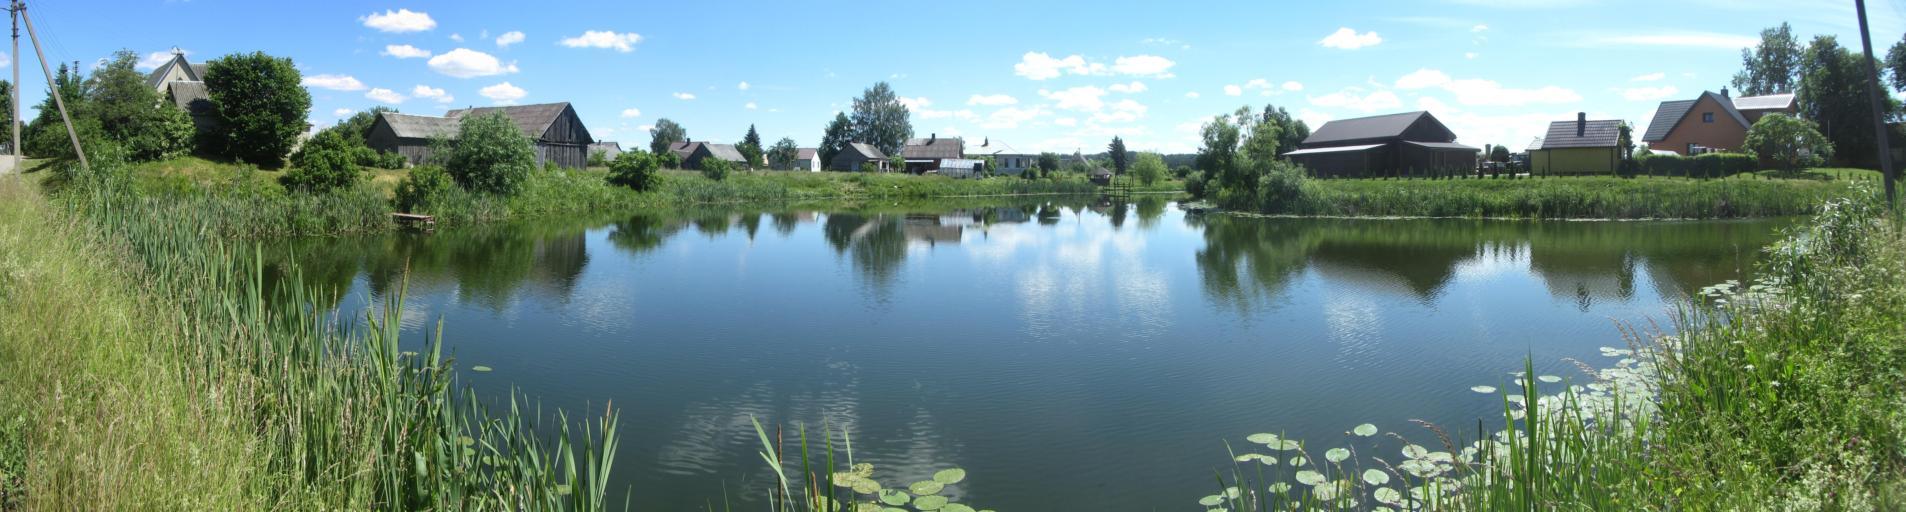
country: LT
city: Birstonas
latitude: 54.7343
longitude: 24.1154
